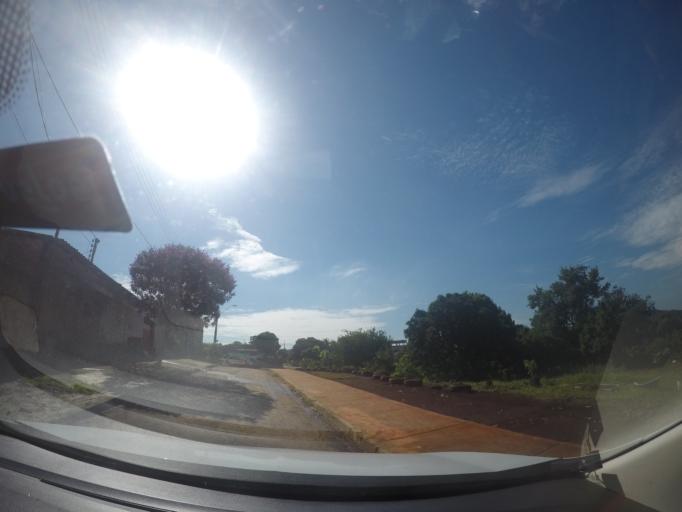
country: BR
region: Goias
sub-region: Goiania
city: Goiania
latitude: -16.6643
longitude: -49.1935
